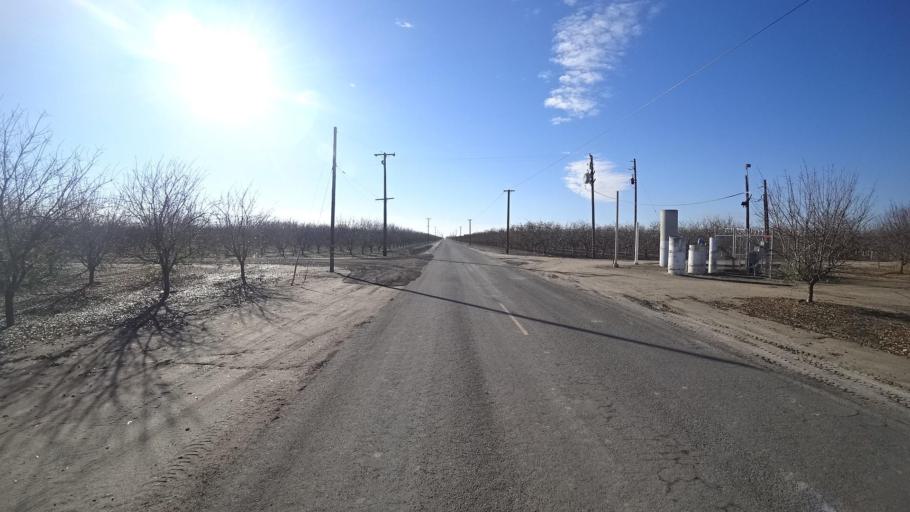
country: US
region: California
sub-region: Kern County
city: Delano
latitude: 35.7397
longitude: -119.3119
